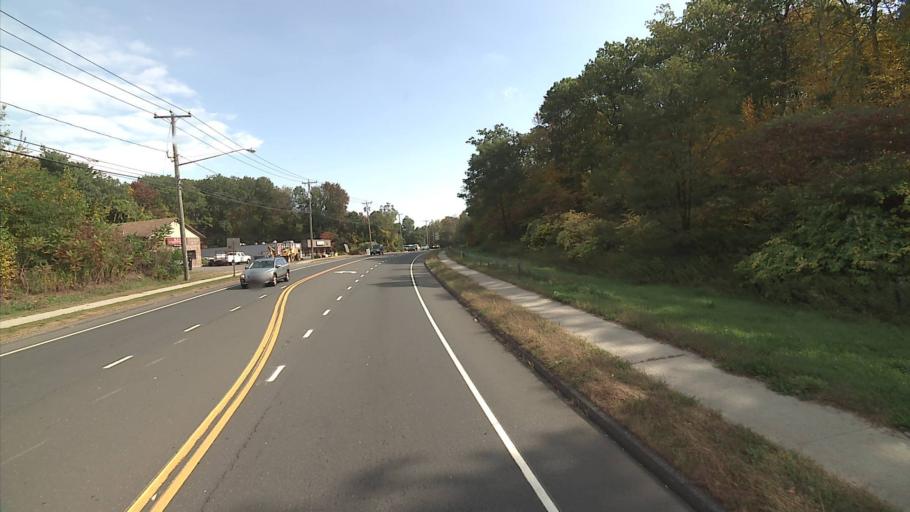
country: US
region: Connecticut
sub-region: Litchfield County
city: Terryville
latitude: 41.6772
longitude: -73.0318
